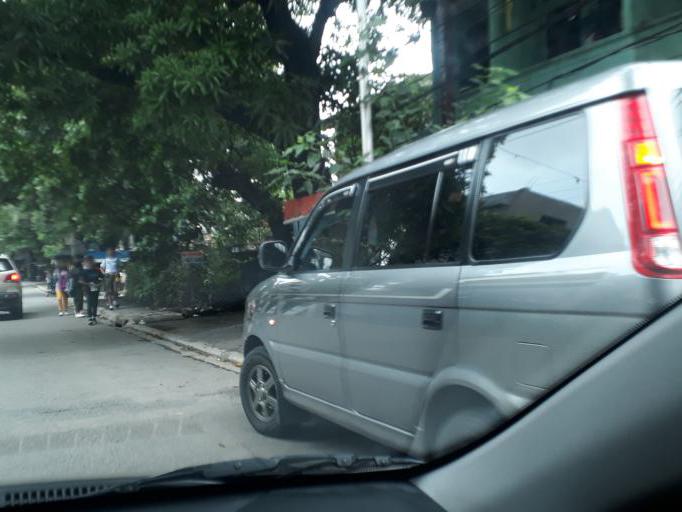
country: PH
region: Calabarzon
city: Del Monte
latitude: 14.6285
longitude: 121.0251
